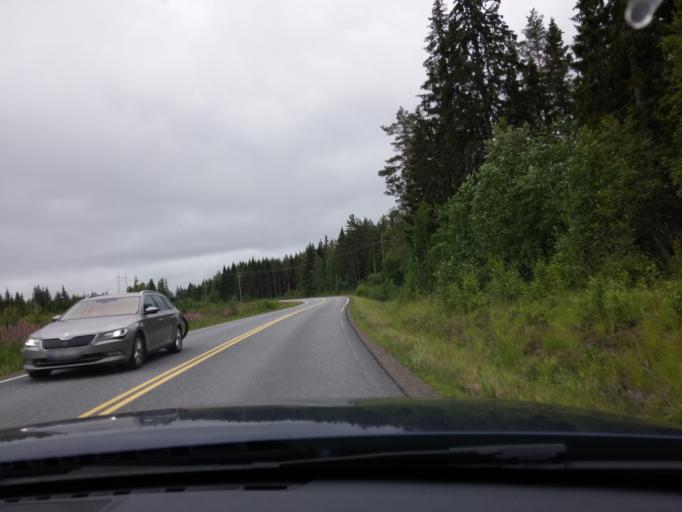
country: FI
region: Central Finland
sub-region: Joutsa
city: Joutsa
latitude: 61.8215
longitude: 25.9212
